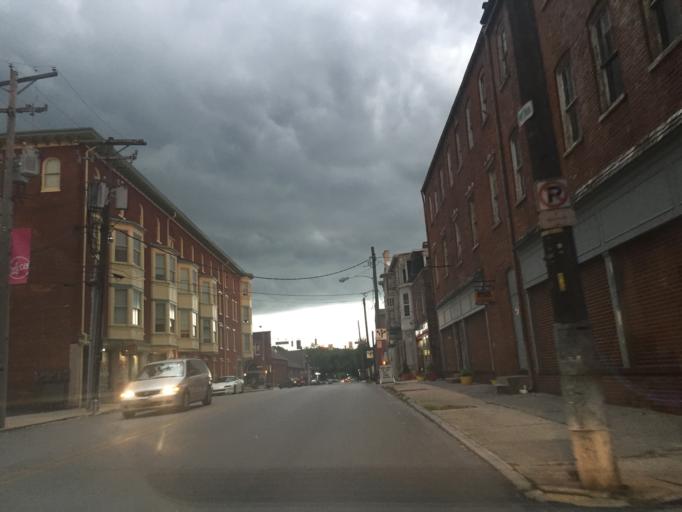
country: US
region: Pennsylvania
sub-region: York County
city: York
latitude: 39.9603
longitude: -76.7375
